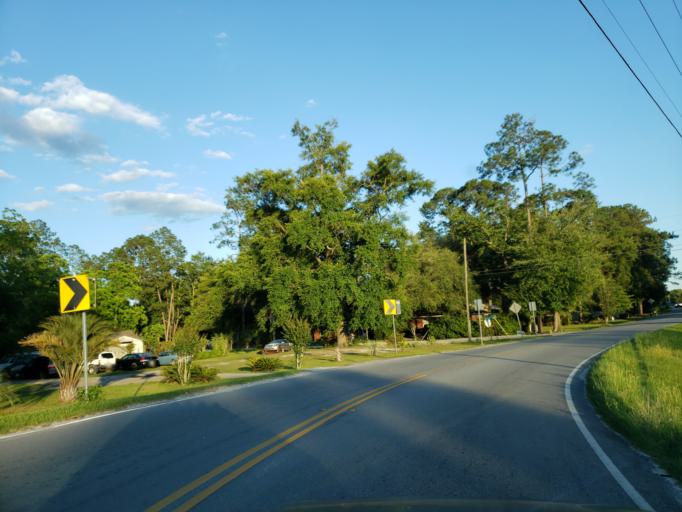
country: US
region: Georgia
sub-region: Lowndes County
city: Valdosta
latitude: 30.7674
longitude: -83.2672
